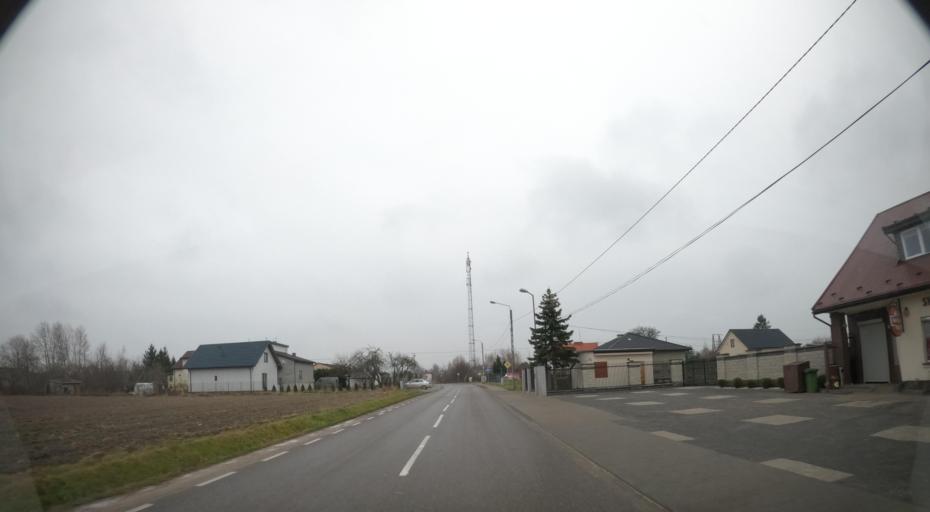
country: PL
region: Masovian Voivodeship
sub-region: Powiat radomski
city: Skaryszew
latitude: 51.3786
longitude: 21.2529
